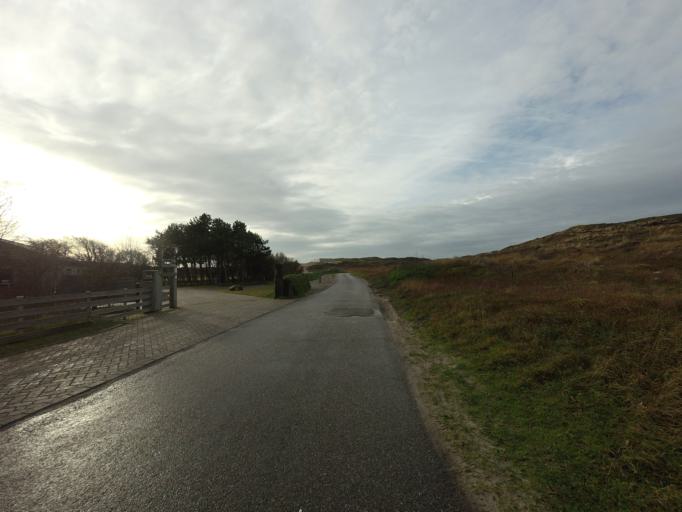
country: NL
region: North Holland
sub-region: Gemeente Den Helder
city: Den Helder
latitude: 53.0234
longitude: 4.7330
